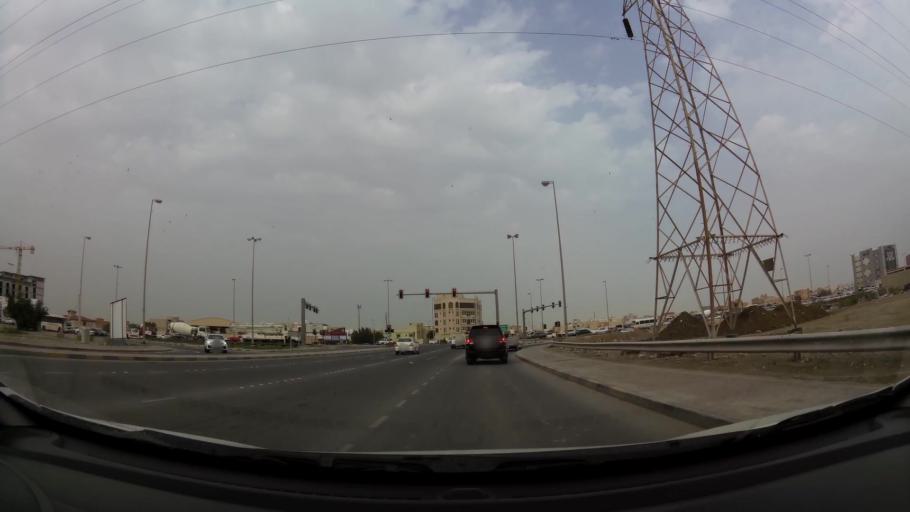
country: BH
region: Northern
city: Ar Rifa'
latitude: 26.1406
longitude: 50.5799
